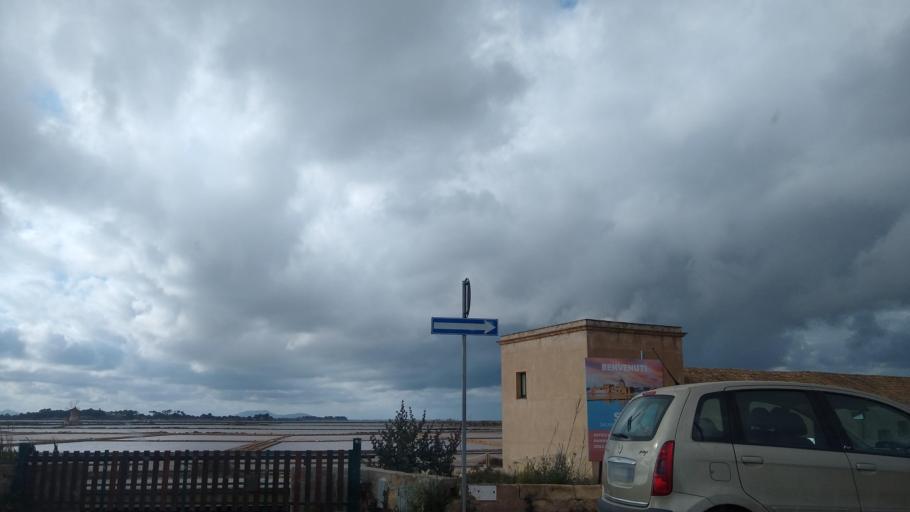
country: IT
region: Sicily
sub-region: Trapani
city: Marsala
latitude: 37.8573
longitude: 12.4841
